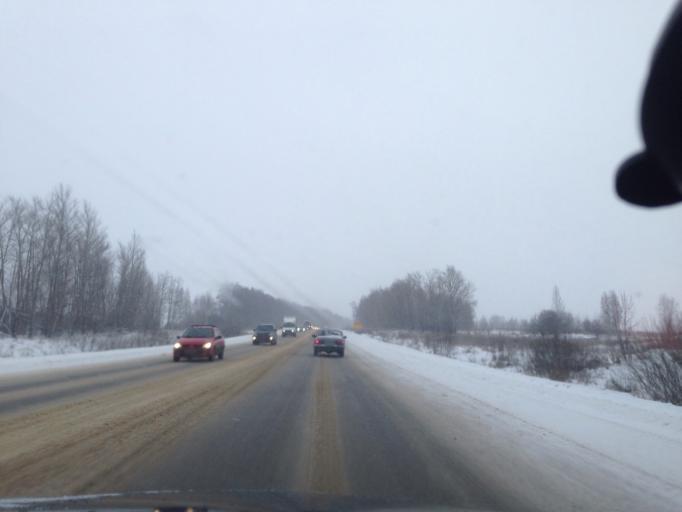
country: RU
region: Tula
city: Bolokhovo
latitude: 54.0760
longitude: 37.7874
